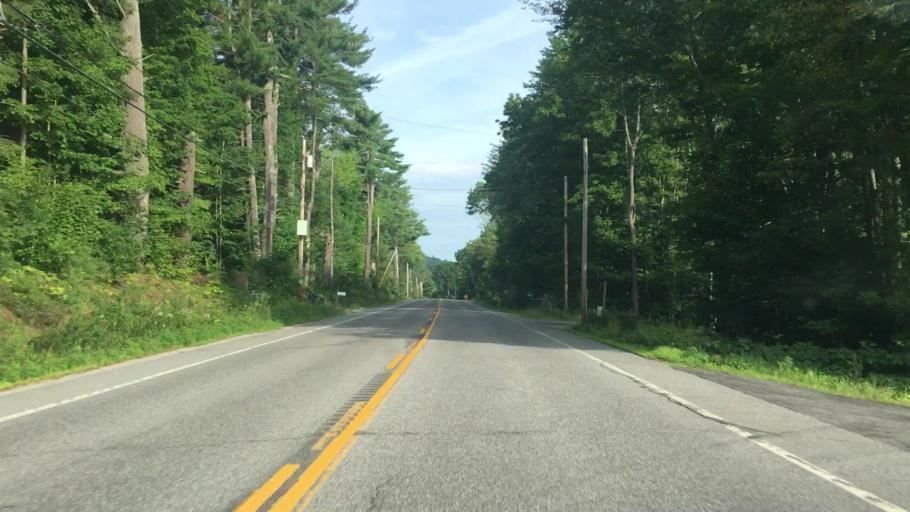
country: US
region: Maine
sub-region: York County
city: Limington
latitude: 43.7543
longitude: -70.6889
